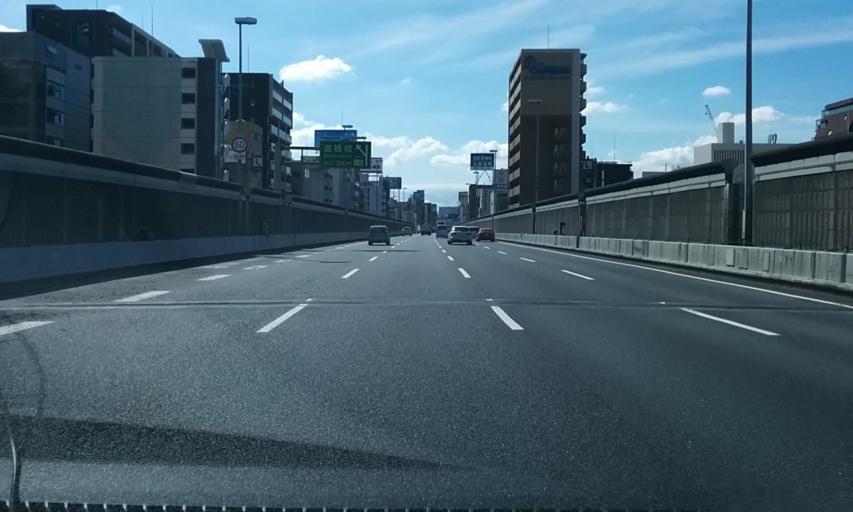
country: JP
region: Osaka
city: Osaka-shi
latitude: 34.6753
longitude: 135.5109
